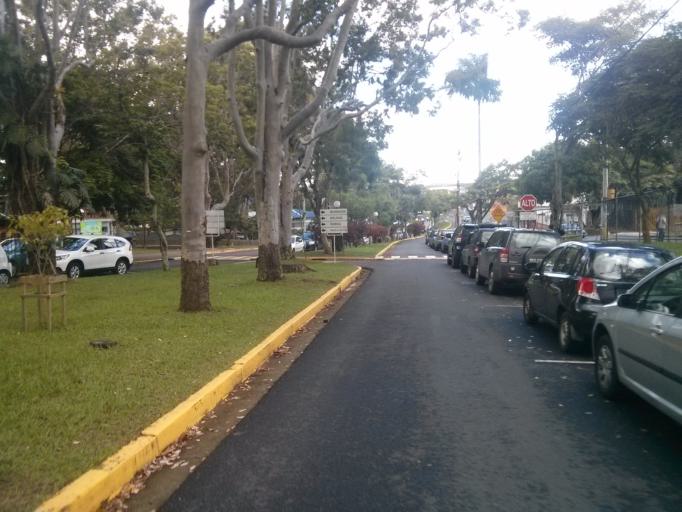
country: CR
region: San Jose
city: San Pedro
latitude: 9.9382
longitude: -84.0483
